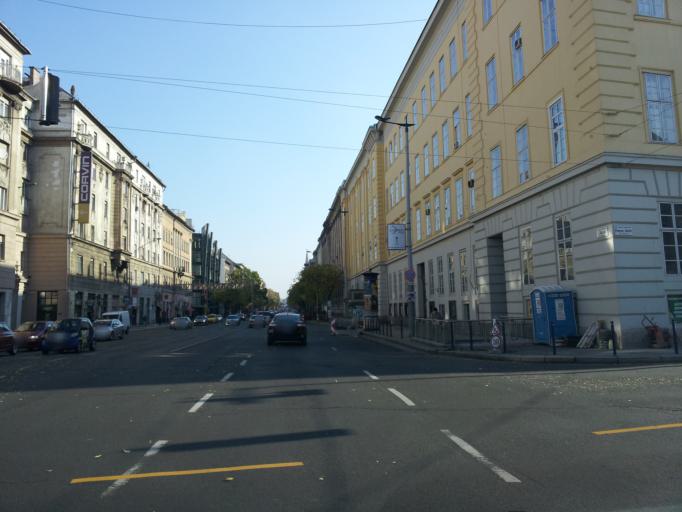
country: HU
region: Budapest
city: Budapest VIII. keruelet
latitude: 47.4857
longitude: 19.0701
